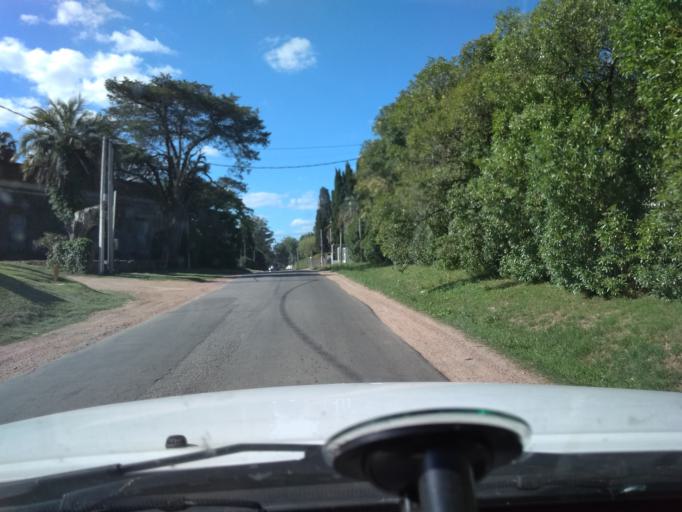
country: UY
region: Canelones
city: La Paz
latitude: -34.8025
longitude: -56.2100
